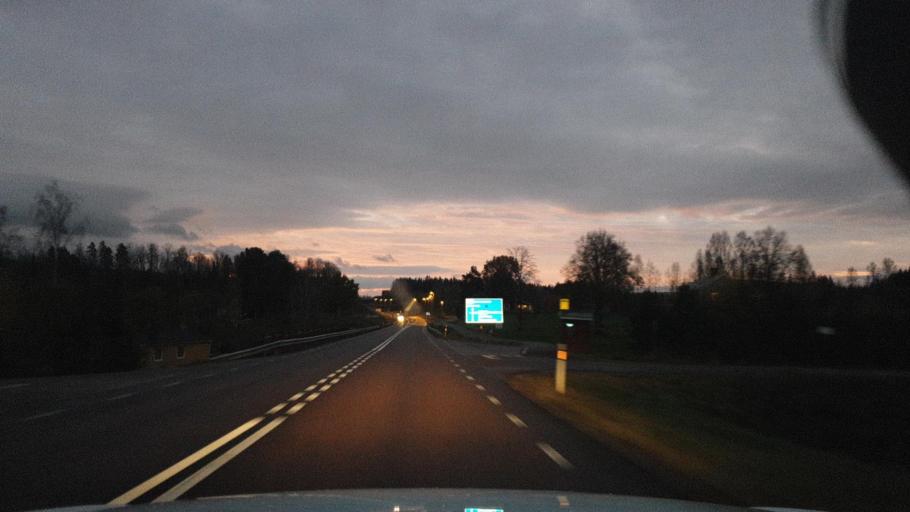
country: SE
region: Vaermland
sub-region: Eda Kommun
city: Amotfors
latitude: 59.7807
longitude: 12.3653
